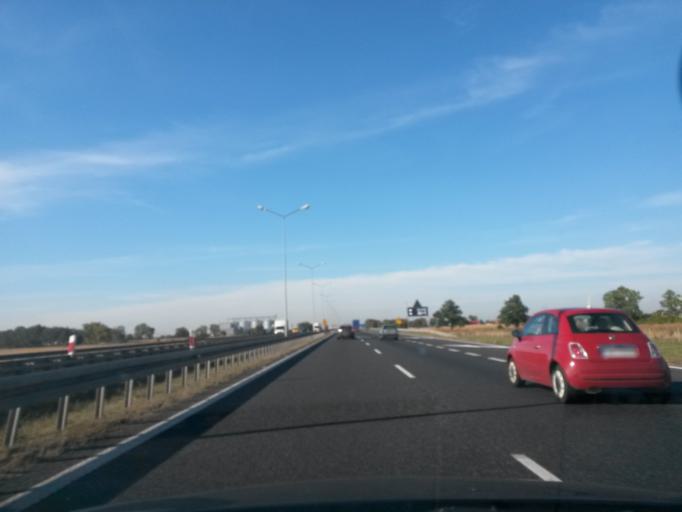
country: PL
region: Lower Silesian Voivodeship
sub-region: Powiat wroclawski
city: Zorawina
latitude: 50.9726
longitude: 17.0634
